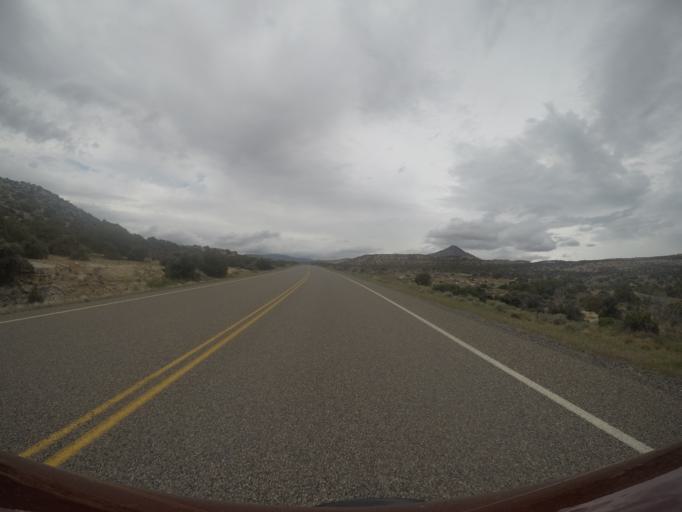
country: US
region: Wyoming
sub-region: Big Horn County
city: Lovell
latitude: 44.9982
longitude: -108.2624
